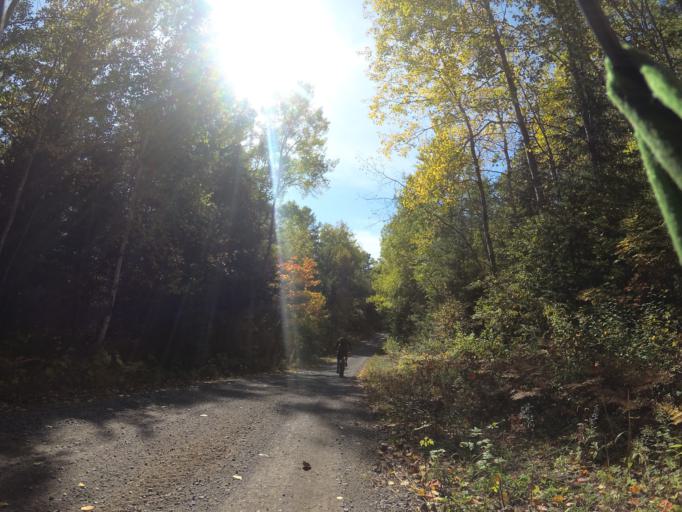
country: CA
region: Ontario
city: Pembroke
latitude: 45.3533
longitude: -77.1581
